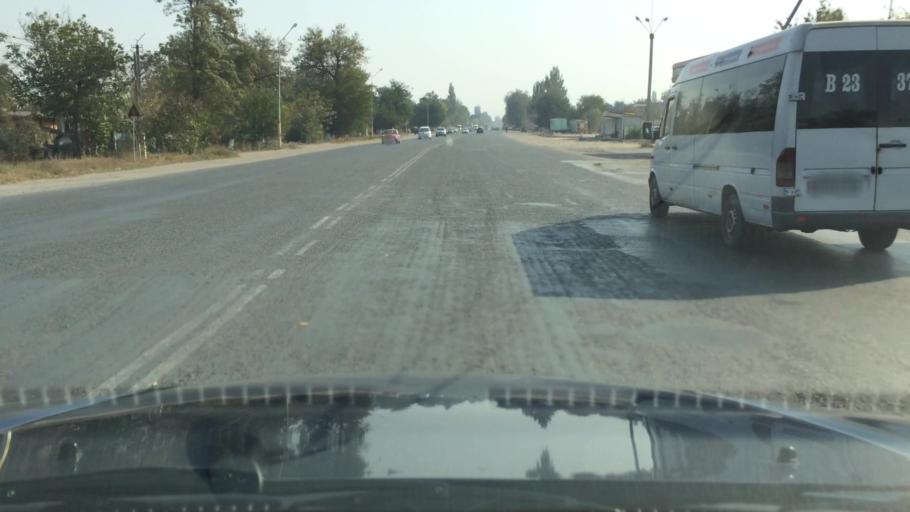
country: KG
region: Chuy
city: Lebedinovka
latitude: 42.8875
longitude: 74.6677
